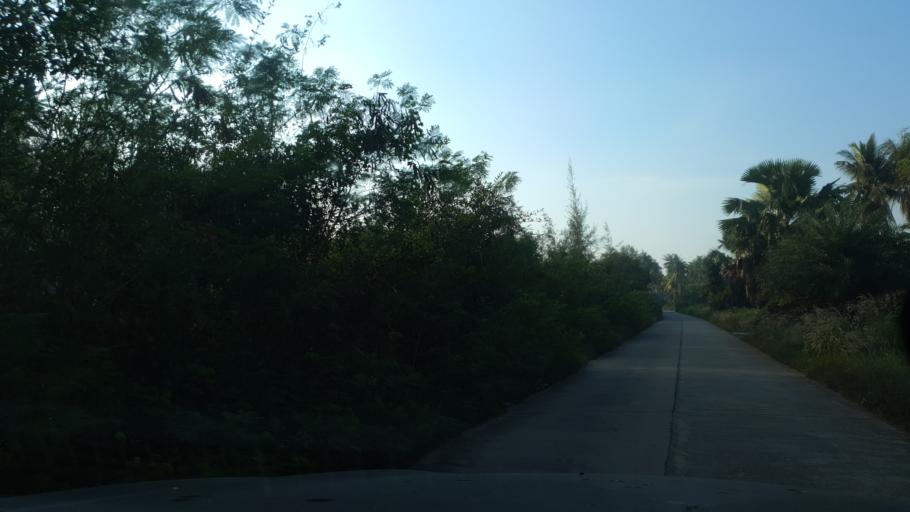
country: TH
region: Prachuap Khiri Khan
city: Bang Saphan
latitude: 11.3024
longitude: 99.5501
